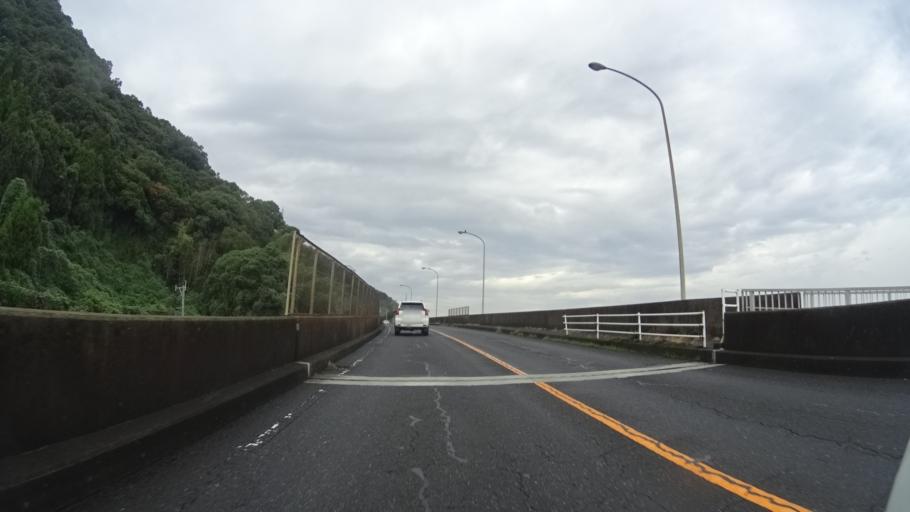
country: JP
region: Kagoshima
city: Kajiki
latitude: 31.6982
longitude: 130.6134
